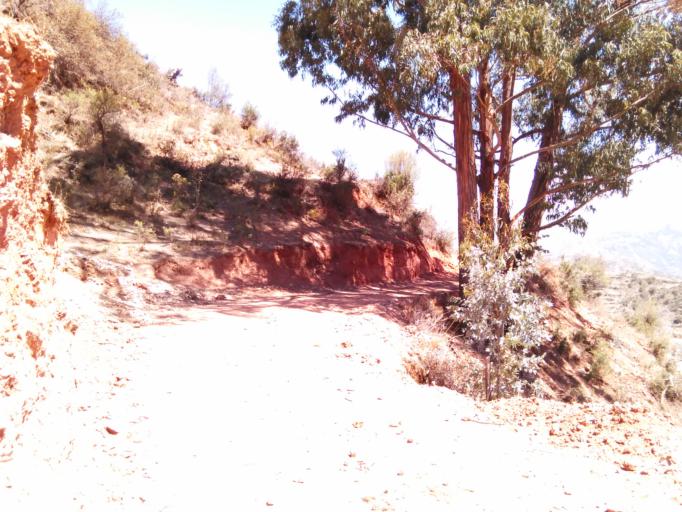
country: PE
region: Ayacucho
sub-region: Provincia de Victor Fajardo
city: Canaria
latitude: -13.8837
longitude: -73.9473
